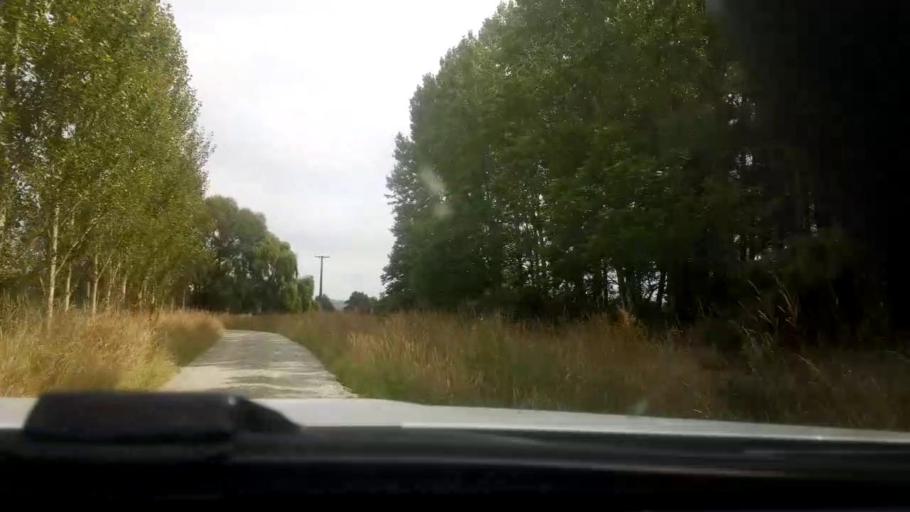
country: NZ
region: Canterbury
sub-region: Timaru District
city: Pleasant Point
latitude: -44.3259
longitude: 171.1954
